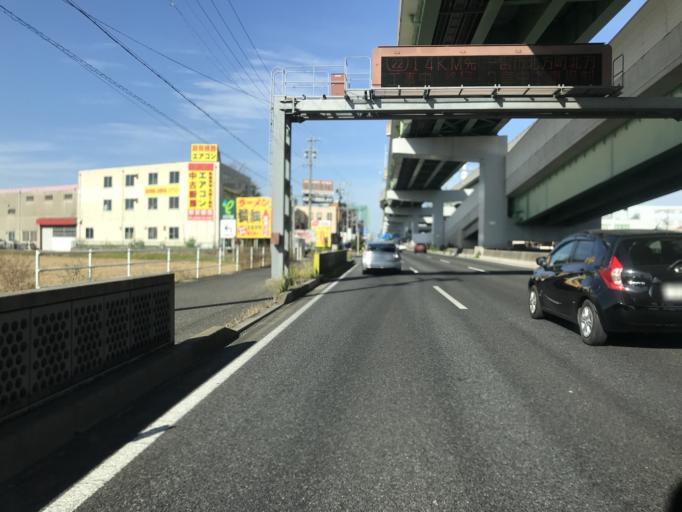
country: JP
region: Aichi
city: Iwakura
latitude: 35.2523
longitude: 136.8436
